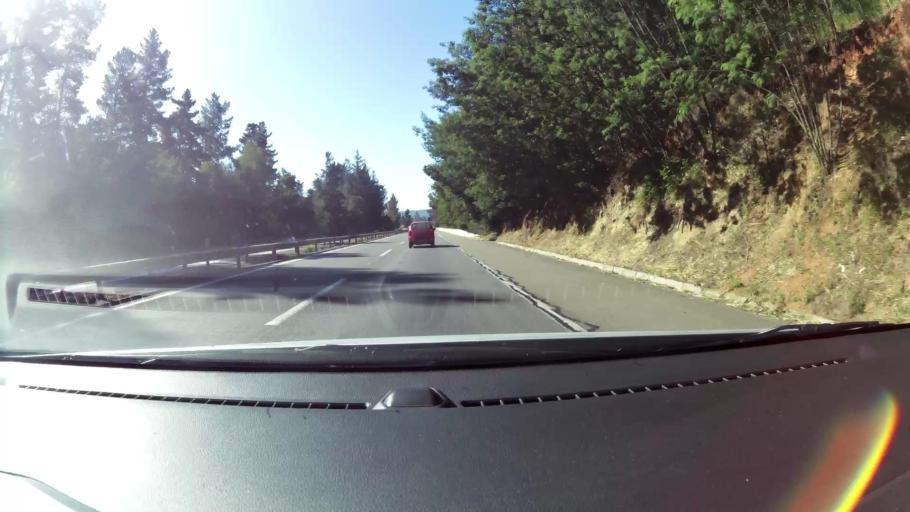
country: CL
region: Valparaiso
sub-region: Provincia de Valparaiso
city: Vina del Mar
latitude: -33.1514
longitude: -71.5575
